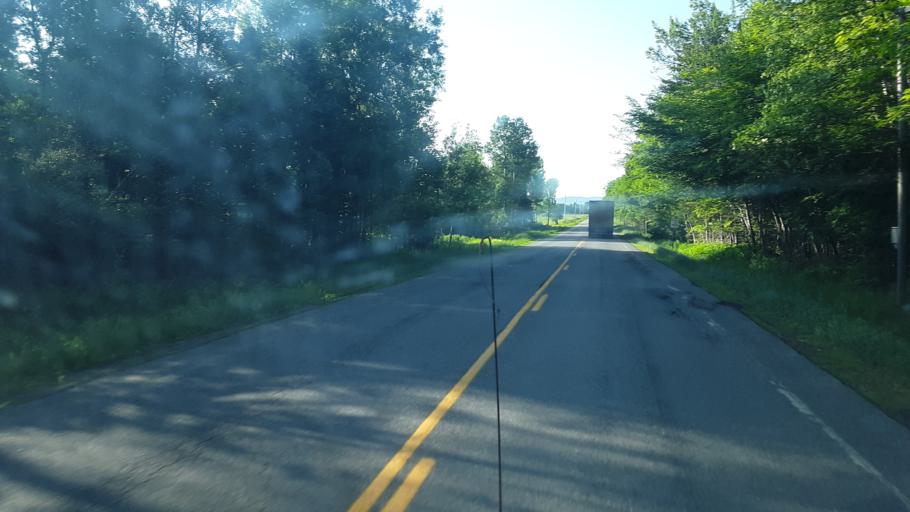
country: US
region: Maine
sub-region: Penobscot County
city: Patten
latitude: 46.1603
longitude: -68.2261
